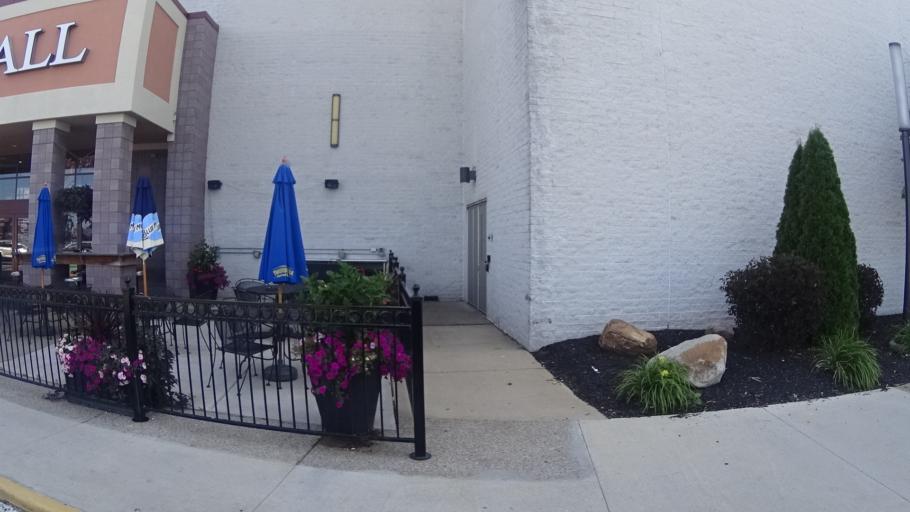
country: US
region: Ohio
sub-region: Erie County
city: Sandusky
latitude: 41.4177
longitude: -82.6699
